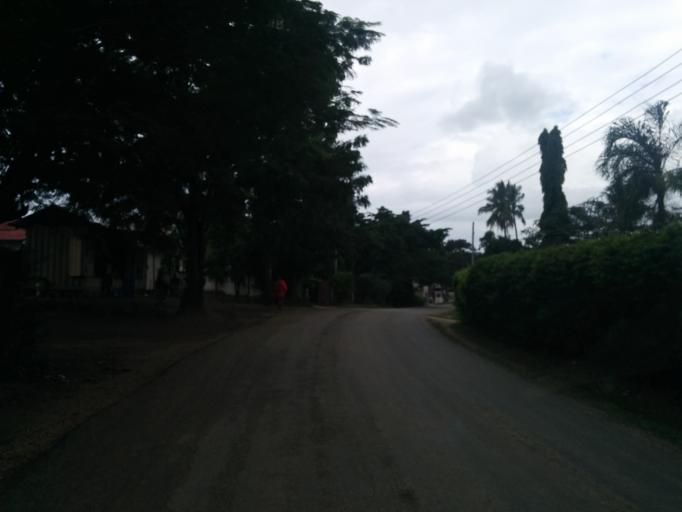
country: TZ
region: Dar es Salaam
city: Magomeni
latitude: -6.7697
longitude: 39.1913
